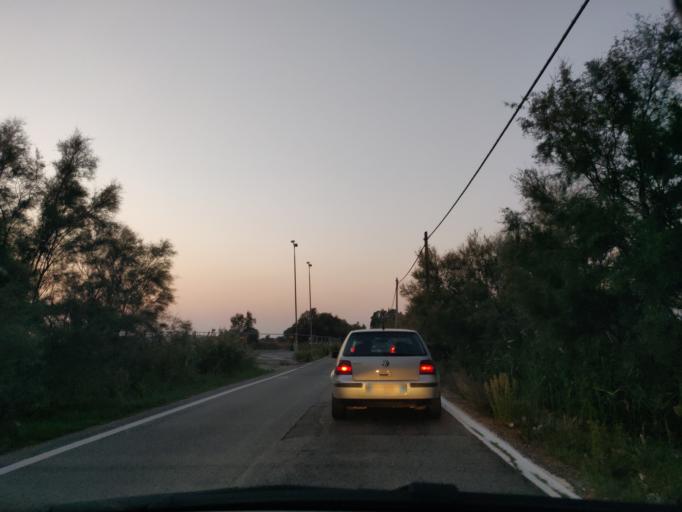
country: IT
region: Latium
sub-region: Citta metropolitana di Roma Capitale
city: Npp 23 (Parco Leonardo)
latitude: 41.8238
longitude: 12.2911
